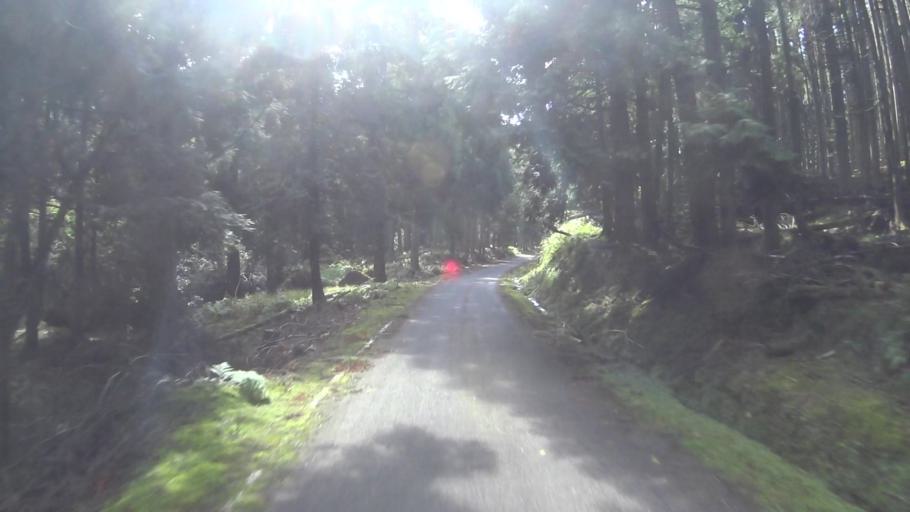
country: JP
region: Hyogo
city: Toyooka
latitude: 35.6114
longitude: 134.9927
